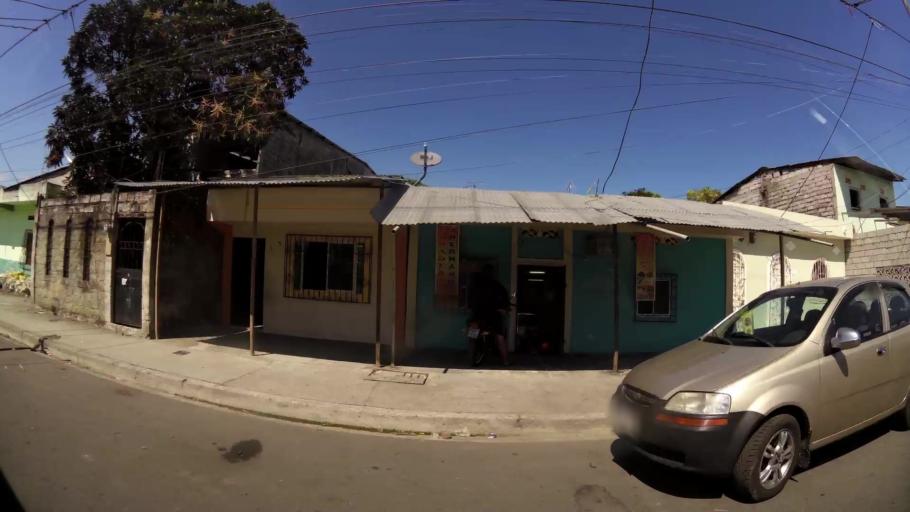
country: EC
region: Guayas
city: Guayaquil
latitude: -2.2219
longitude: -79.9467
